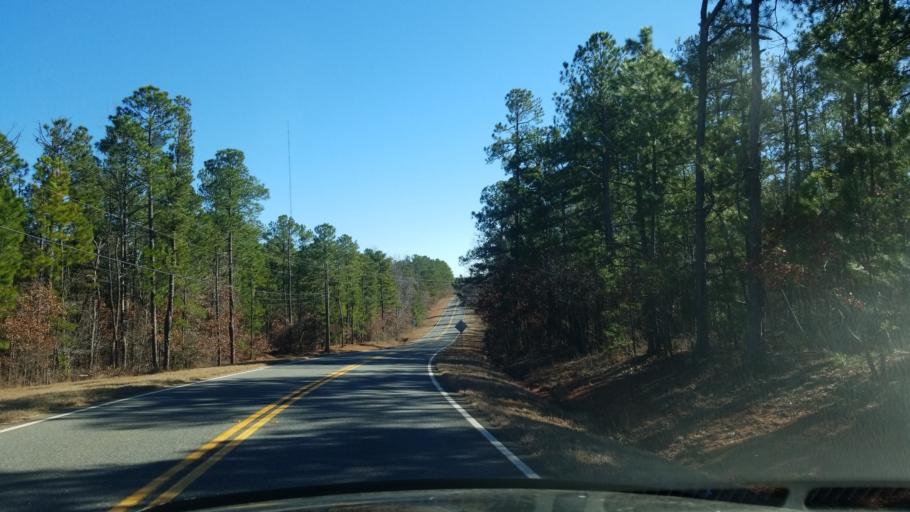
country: US
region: Georgia
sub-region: Meriwether County
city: Manchester
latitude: 32.8490
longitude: -84.6974
